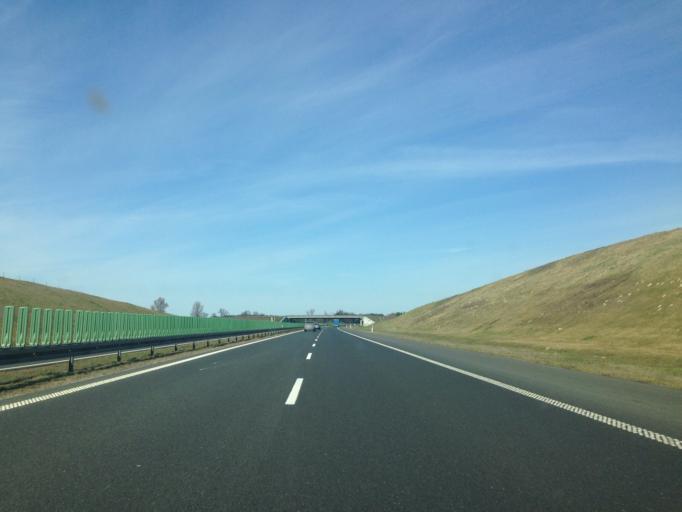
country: PL
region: Pomeranian Voivodeship
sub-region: Powiat starogardzki
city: Smetowo Graniczne
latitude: 53.7933
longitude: 18.6265
